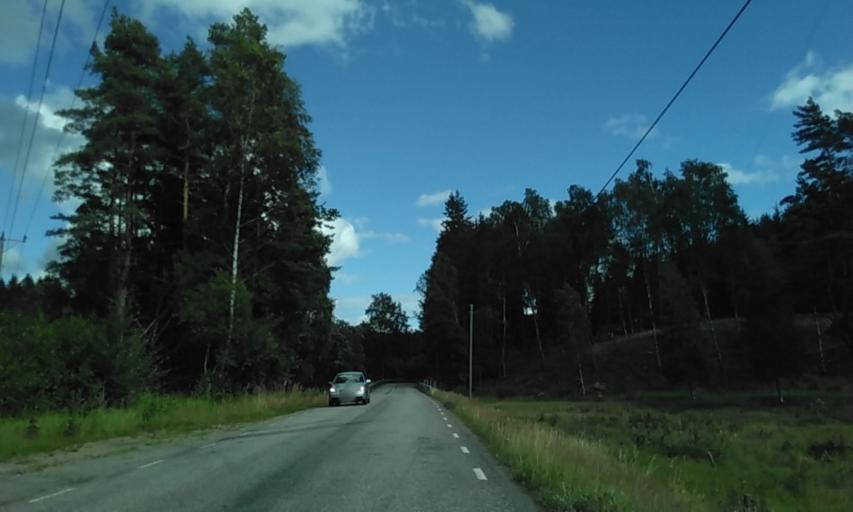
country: SE
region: Vaestra Goetaland
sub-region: Vargarda Kommun
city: Jonstorp
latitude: 57.9376
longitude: 12.7050
